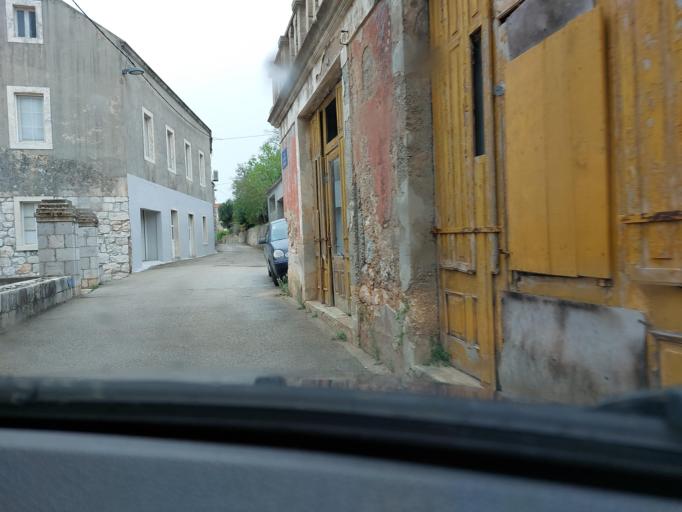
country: HR
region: Dubrovacko-Neretvanska
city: Smokvica
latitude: 42.7665
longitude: 16.8986
